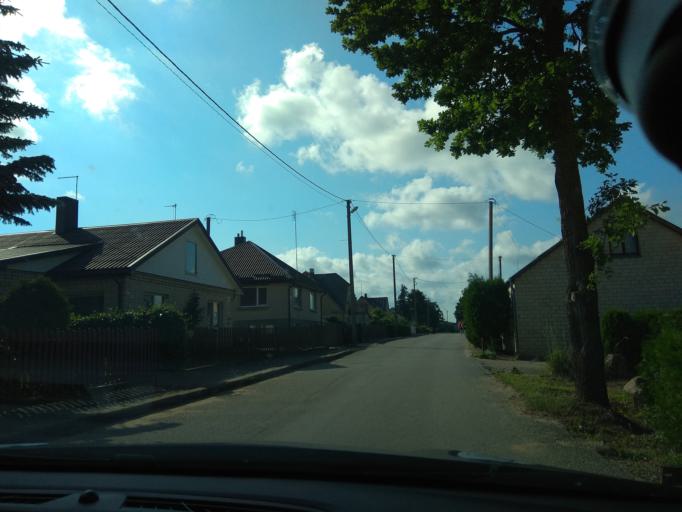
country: LT
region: Siauliu apskritis
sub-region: Joniskis
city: Joniskis
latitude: 56.2467
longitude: 23.6229
